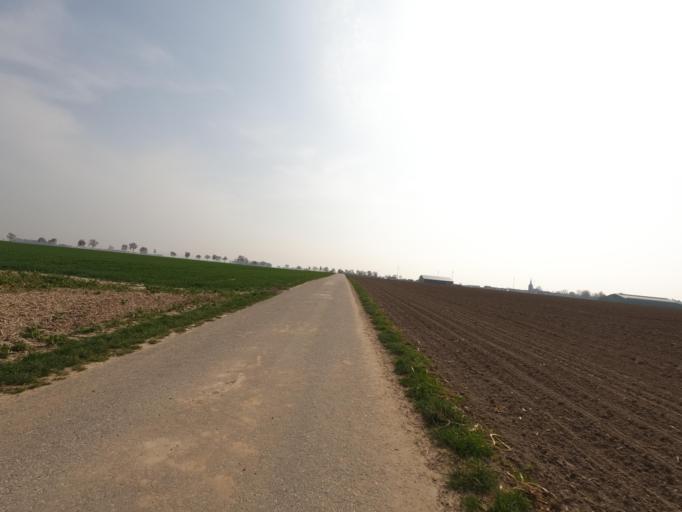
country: DE
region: North Rhine-Westphalia
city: Erkelenz
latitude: 51.0421
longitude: 6.3604
